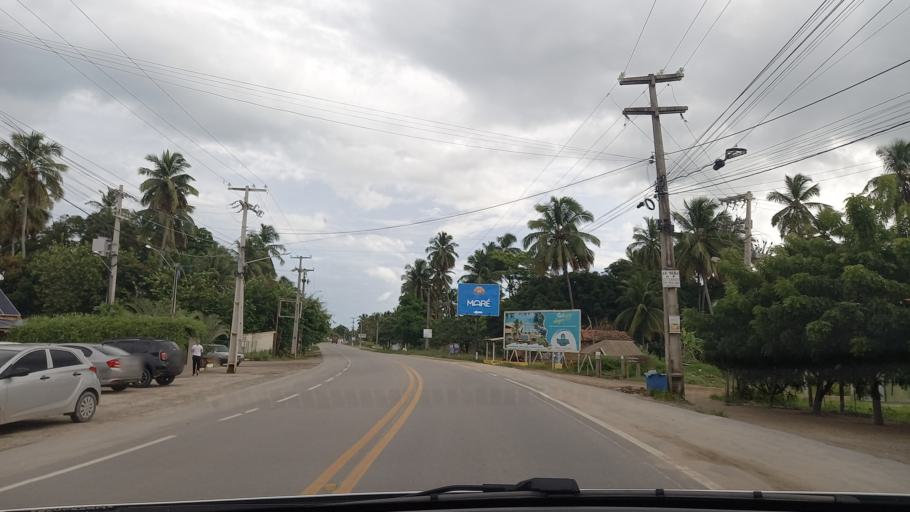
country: BR
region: Pernambuco
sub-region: Sao Jose Da Coroa Grande
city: Sao Jose da Coroa Grande
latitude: -8.9306
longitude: -35.1667
